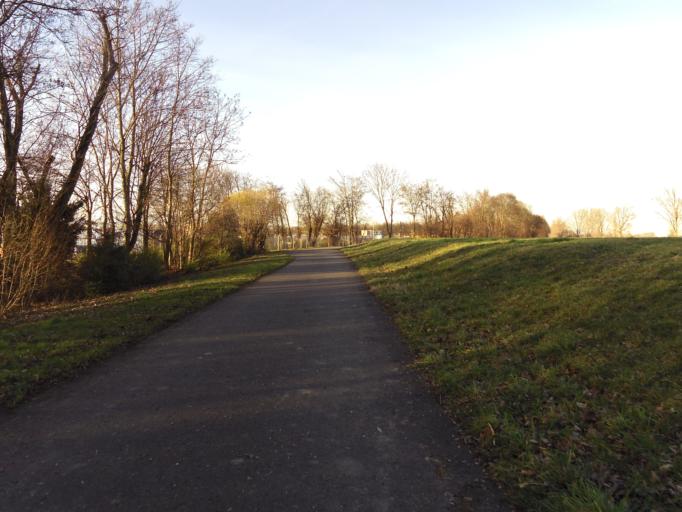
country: DE
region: Rheinland-Pfalz
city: Frankenthal
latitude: 49.5518
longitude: 8.4110
